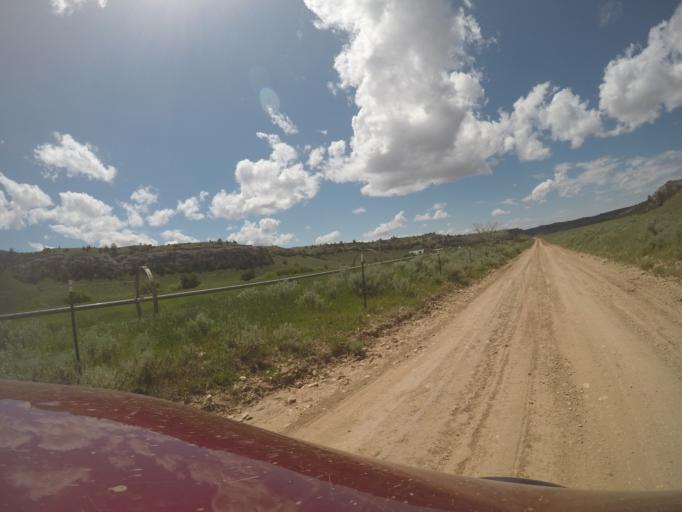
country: US
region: Montana
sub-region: Yellowstone County
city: Laurel
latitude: 45.2378
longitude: -108.6265
